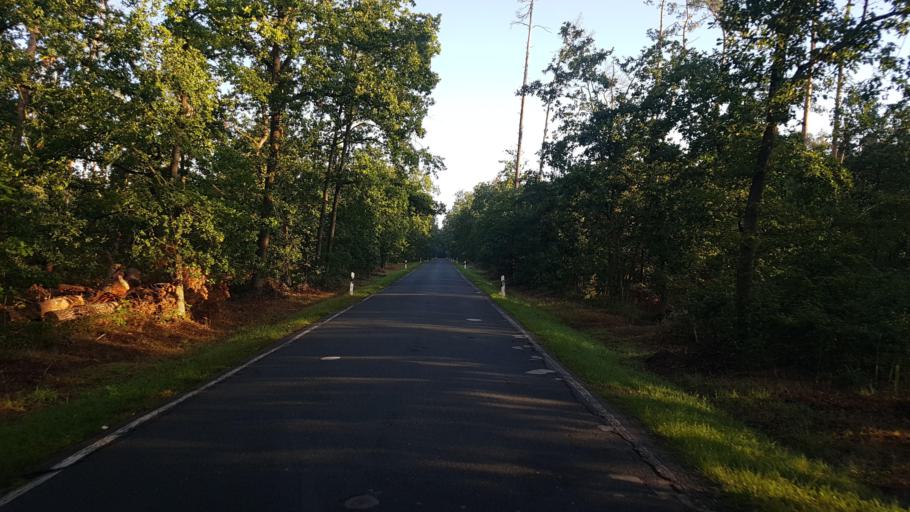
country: DE
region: Saxony-Anhalt
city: Holzdorf
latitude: 51.8335
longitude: 13.0867
